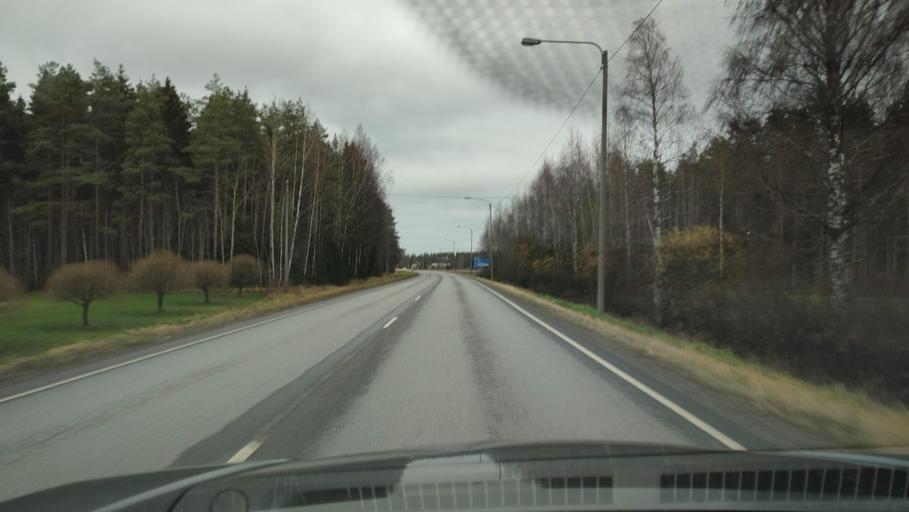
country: FI
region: Southern Ostrobothnia
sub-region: Seinaejoki
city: Kurikka
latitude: 62.6792
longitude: 22.4750
